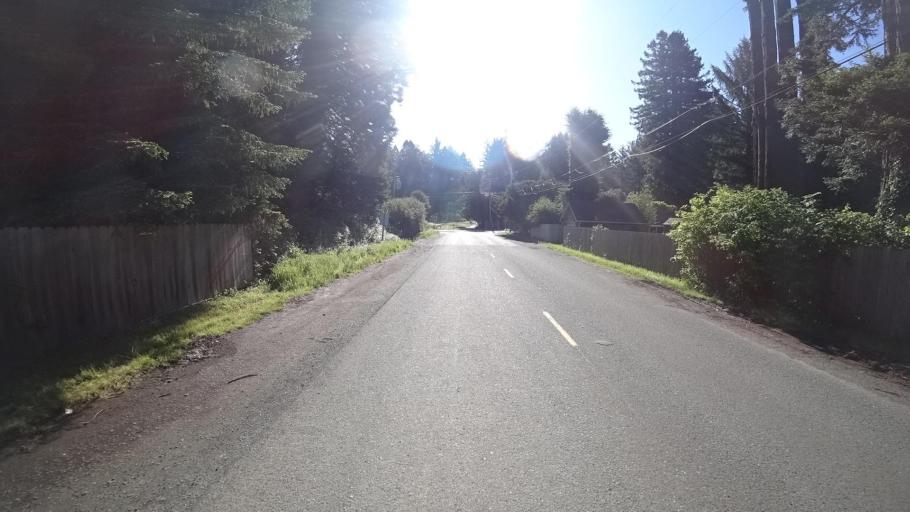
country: US
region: California
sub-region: Humboldt County
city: Westhaven-Moonstone
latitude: 41.0358
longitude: -124.1084
